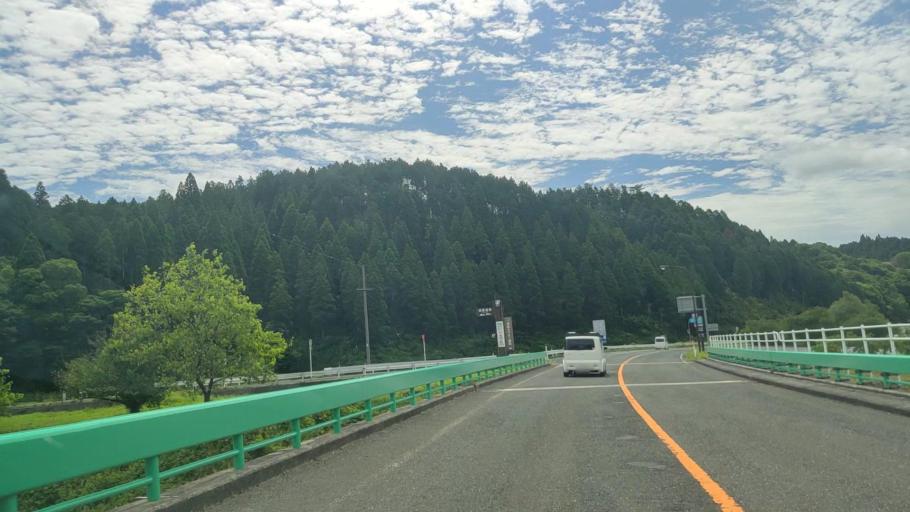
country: JP
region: Okayama
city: Niimi
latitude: 35.1789
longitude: 133.5690
